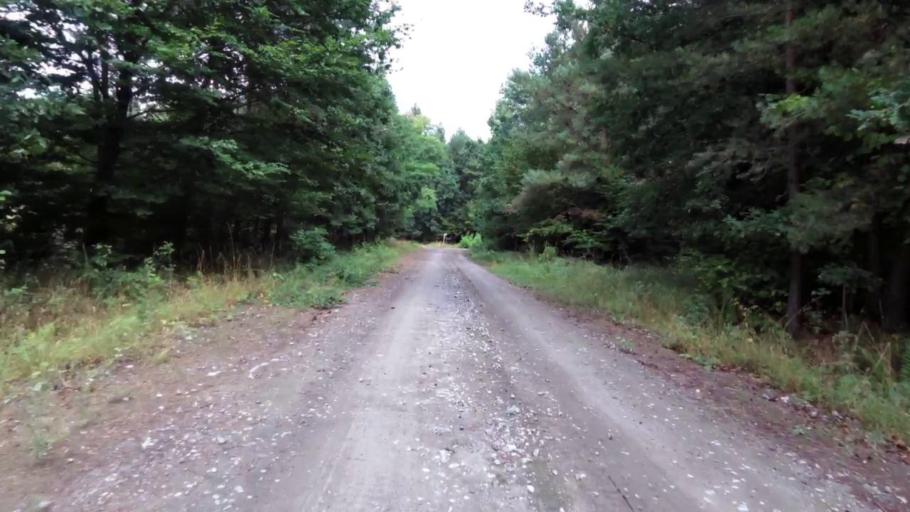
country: PL
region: West Pomeranian Voivodeship
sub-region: Powiat mysliborski
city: Debno
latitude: 52.8656
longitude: 14.6968
